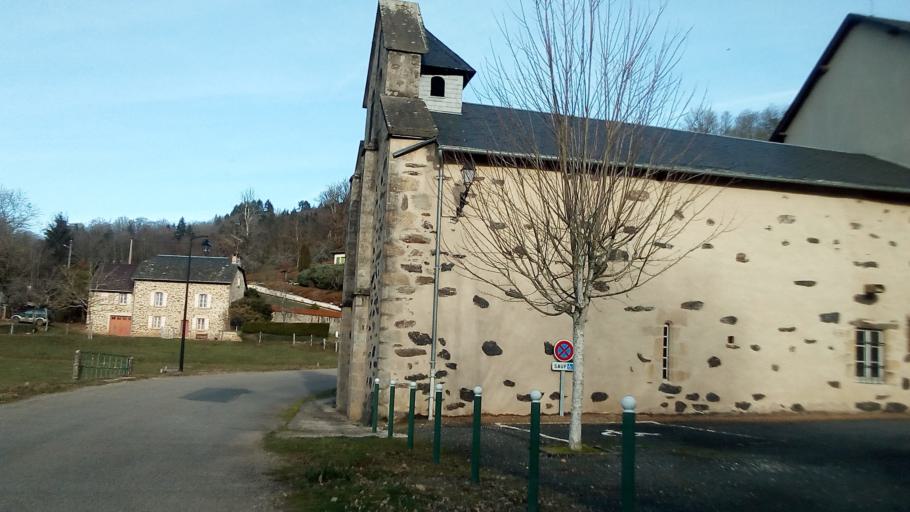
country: FR
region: Limousin
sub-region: Departement de la Correze
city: Naves
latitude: 45.3069
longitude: 1.7965
